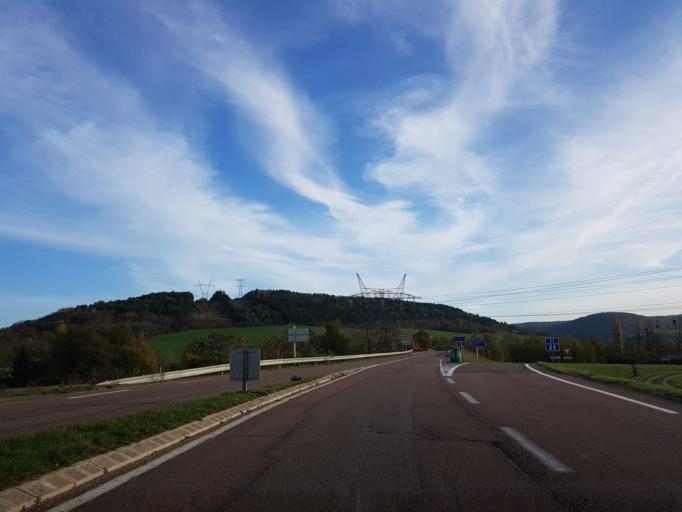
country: FR
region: Bourgogne
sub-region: Departement de la Cote-d'Or
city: Fleurey-sur-Ouche
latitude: 47.3082
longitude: 4.7318
